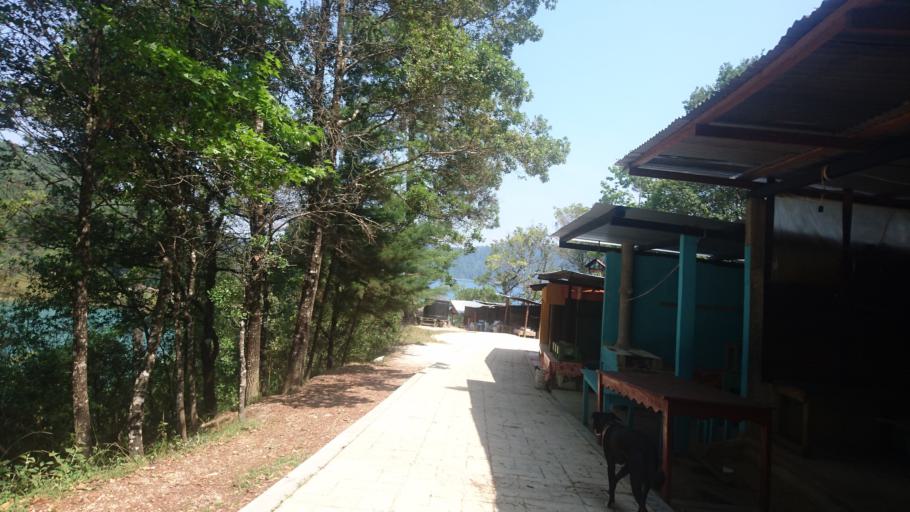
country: GT
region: Huehuetenango
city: Union
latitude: 16.0743
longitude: -91.6804
